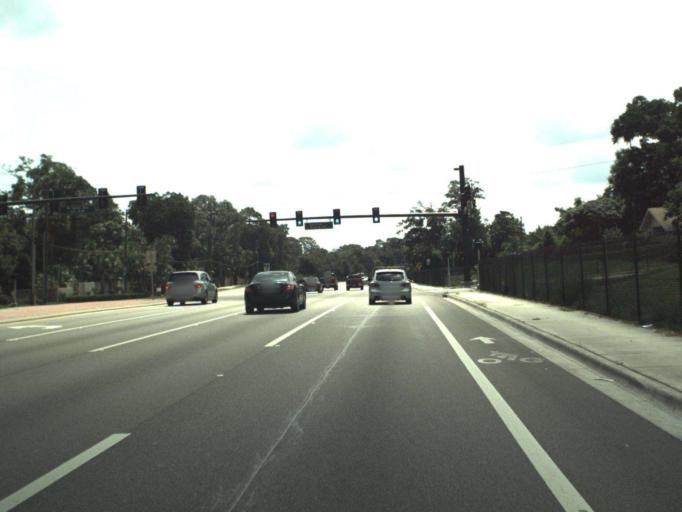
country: US
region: Florida
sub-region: Seminole County
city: Wekiwa Springs
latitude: 28.6871
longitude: -81.4017
